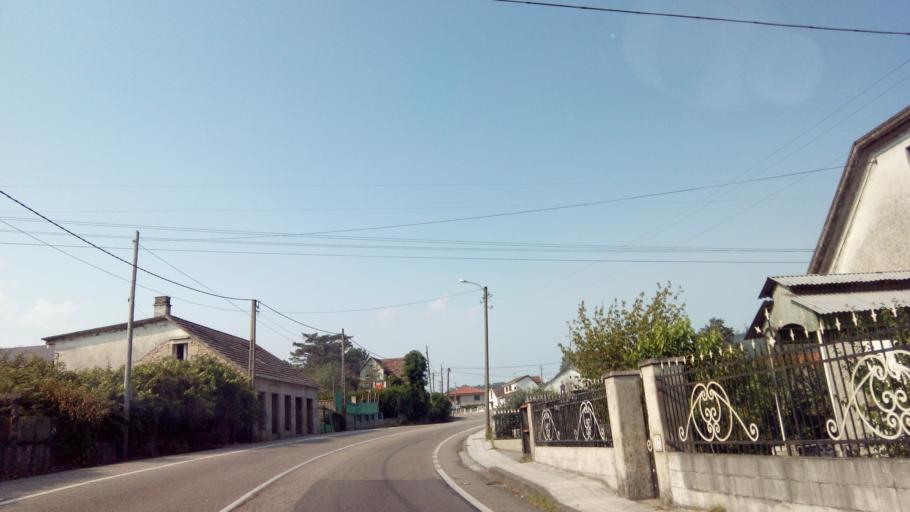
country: ES
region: Galicia
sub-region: Provincia de Pontevedra
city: Ponteareas
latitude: 42.1837
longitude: -8.5072
